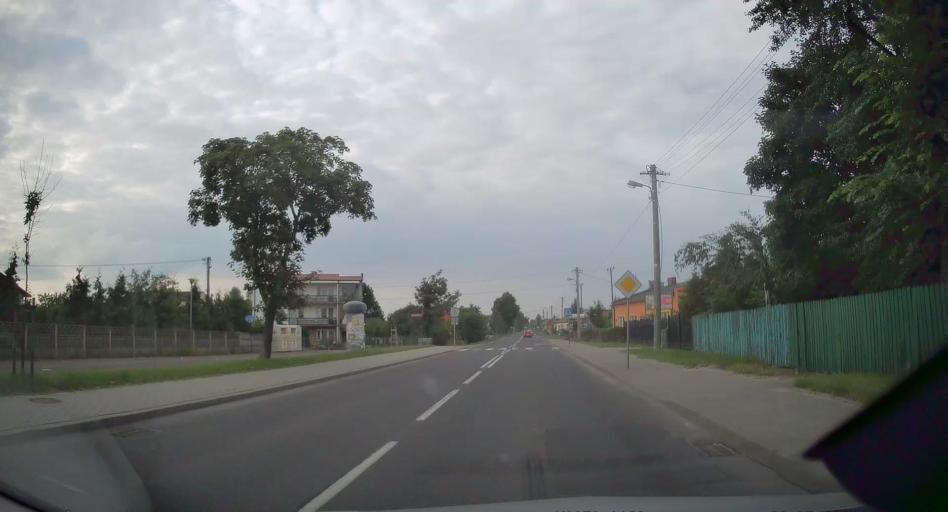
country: PL
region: Lodz Voivodeship
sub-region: Powiat radomszczanski
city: Radomsko
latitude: 51.0919
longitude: 19.4573
